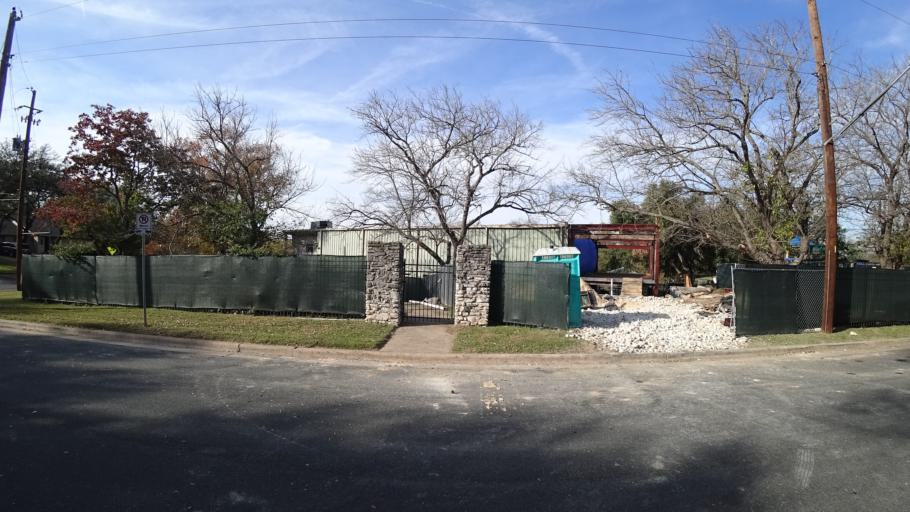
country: US
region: Texas
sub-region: Williamson County
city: Jollyville
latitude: 30.3822
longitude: -97.7519
